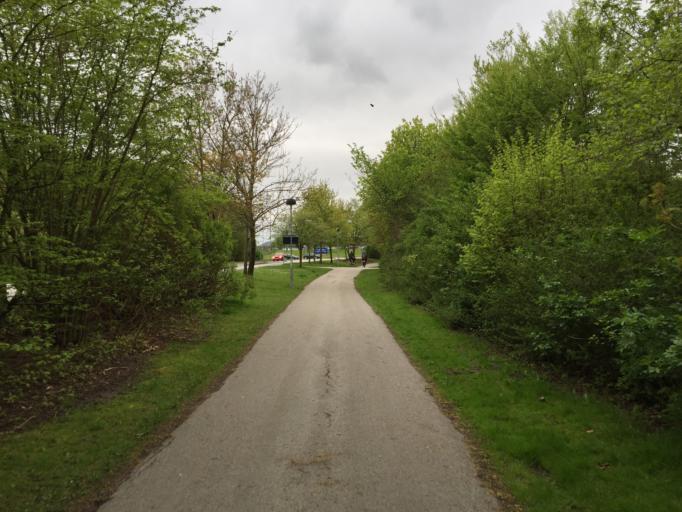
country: SE
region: Skane
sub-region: Lunds Kommun
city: Lund
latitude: 55.7211
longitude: 13.1606
